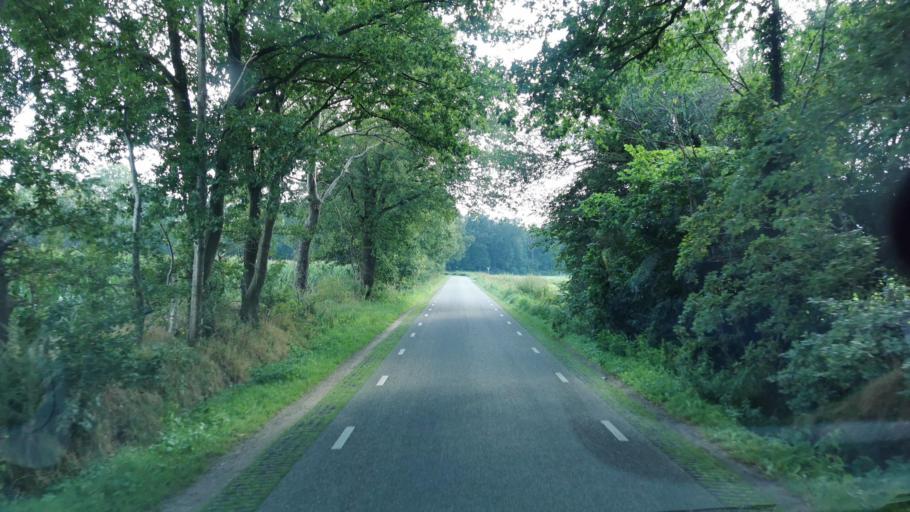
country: NL
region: Overijssel
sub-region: Gemeente Hengelo
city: Hengelo
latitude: 52.3218
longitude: 6.8283
